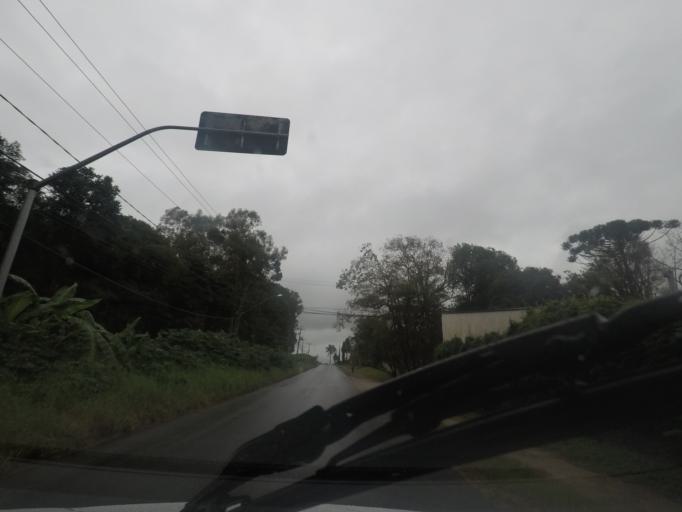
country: BR
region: Parana
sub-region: Quatro Barras
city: Quatro Barras
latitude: -25.3863
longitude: -49.1383
